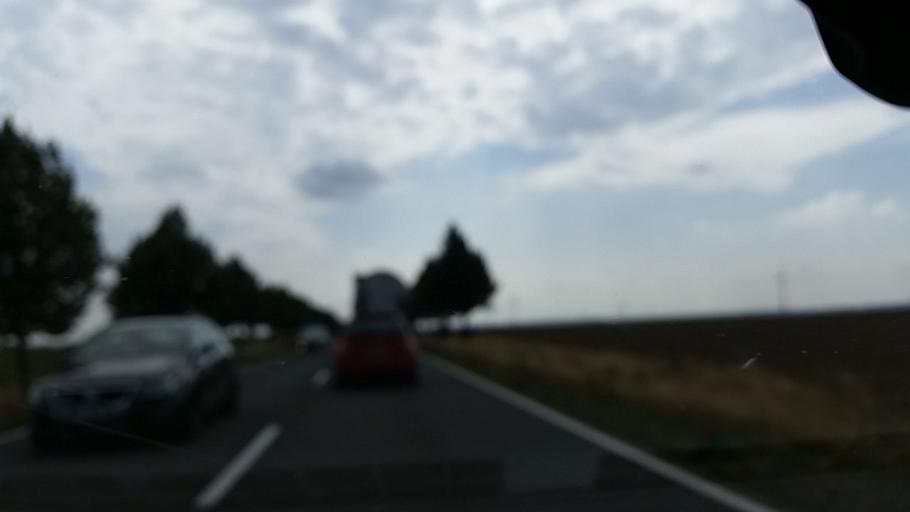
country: DE
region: Saxony-Anhalt
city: Steigra
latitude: 51.3213
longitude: 11.6484
